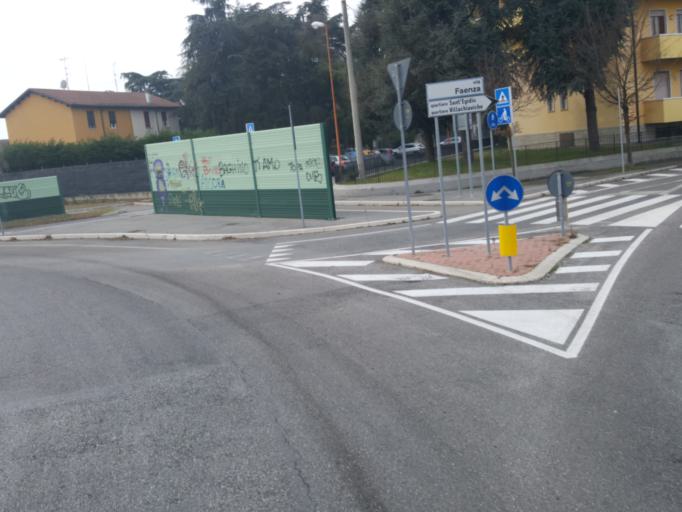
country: IT
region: Emilia-Romagna
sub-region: Forli-Cesena
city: Cesena
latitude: 44.1558
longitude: 12.2691
